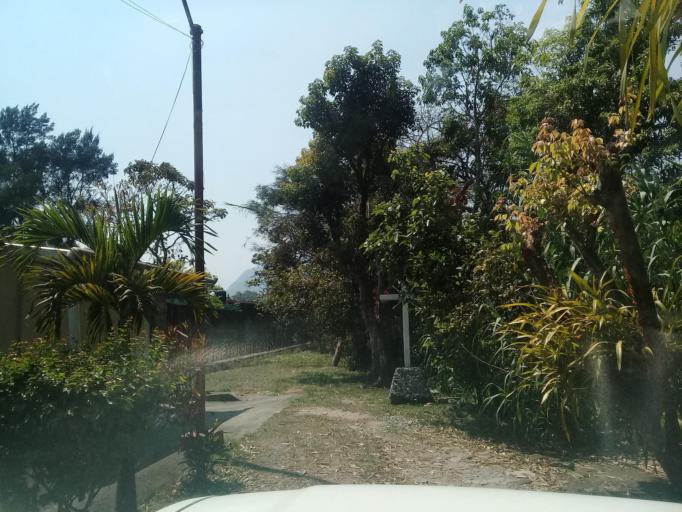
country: MX
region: Veracruz
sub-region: Ixtaczoquitlan
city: Buenavista
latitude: 18.8772
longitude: -97.0517
